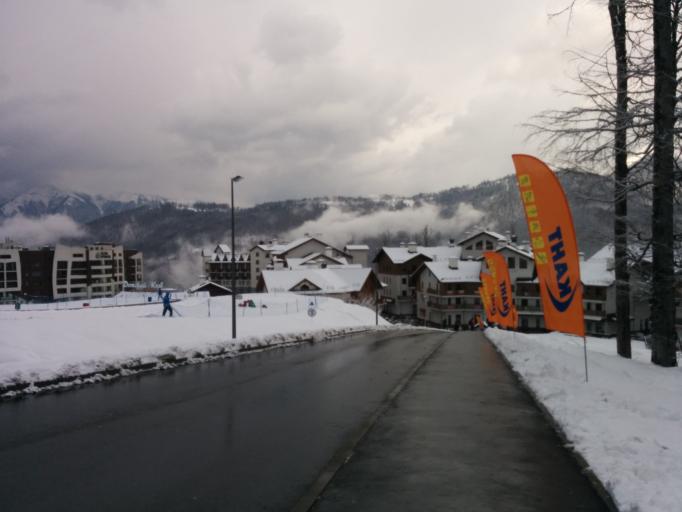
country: RU
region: Krasnodarskiy
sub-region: Sochi City
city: Krasnaya Polyana
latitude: 43.6585
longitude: 40.3201
